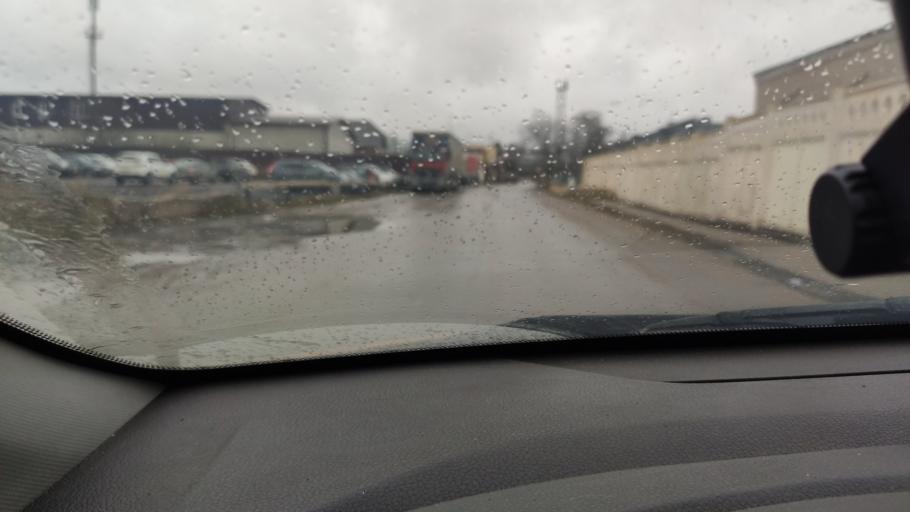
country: RU
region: Moskovskaya
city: Selyatino
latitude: 55.5129
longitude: 36.9673
